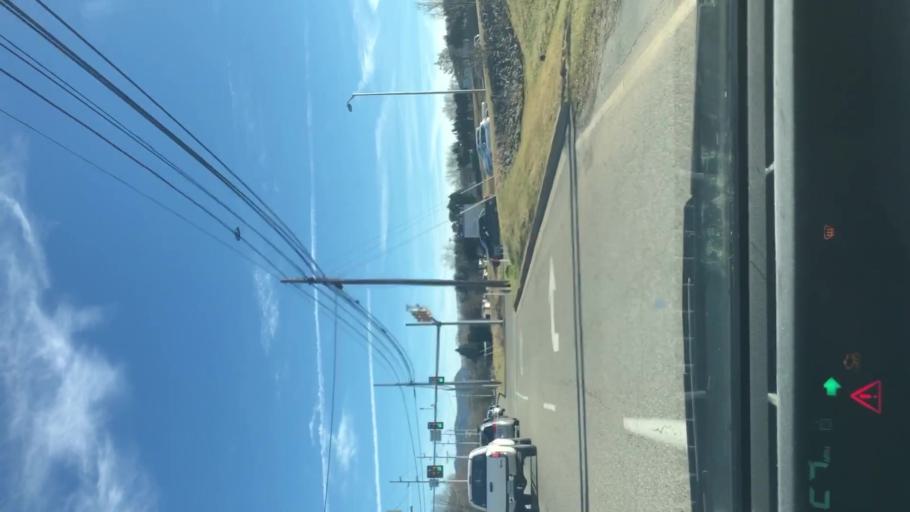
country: US
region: Virginia
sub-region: City of Harrisonburg
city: Harrisonburg
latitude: 38.4375
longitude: -78.8441
